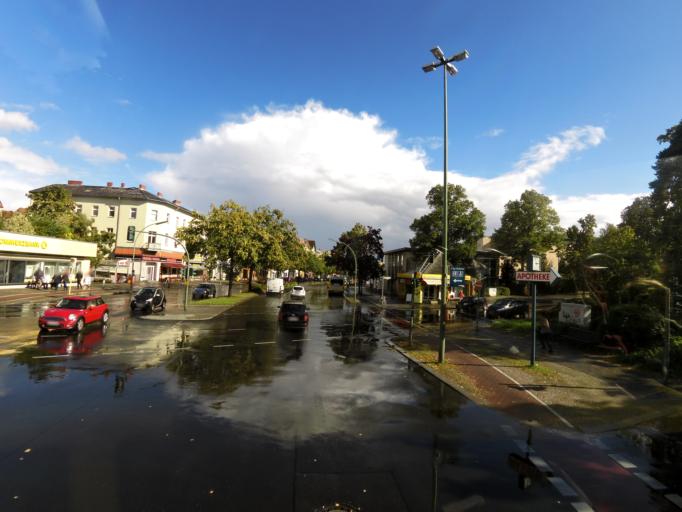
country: DE
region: Berlin
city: Schmargendorf
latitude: 52.4754
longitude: 13.2902
